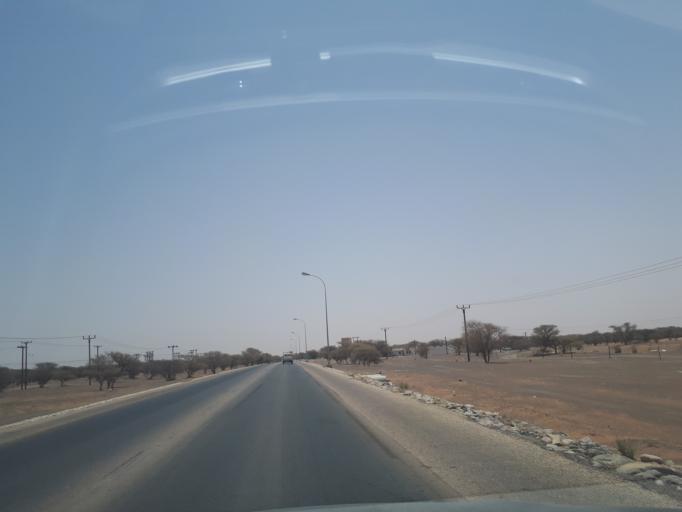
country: OM
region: Ash Sharqiyah
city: Badiyah
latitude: 22.4770
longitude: 58.7831
